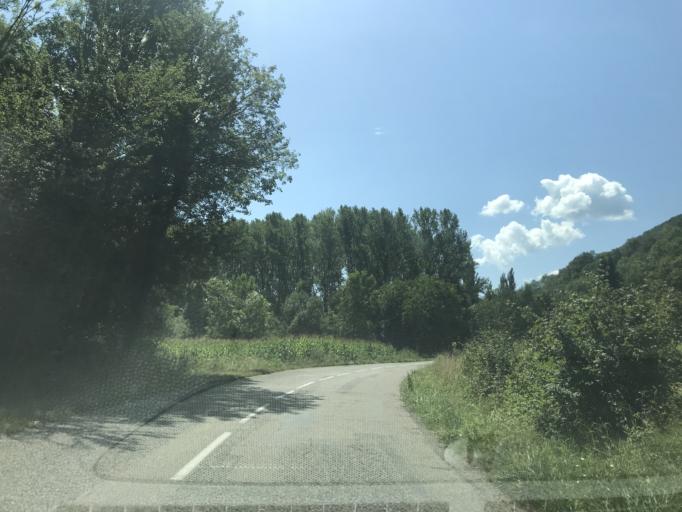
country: FR
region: Rhone-Alpes
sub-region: Departement de la Savoie
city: Chatillon
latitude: 45.8139
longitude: 5.8143
